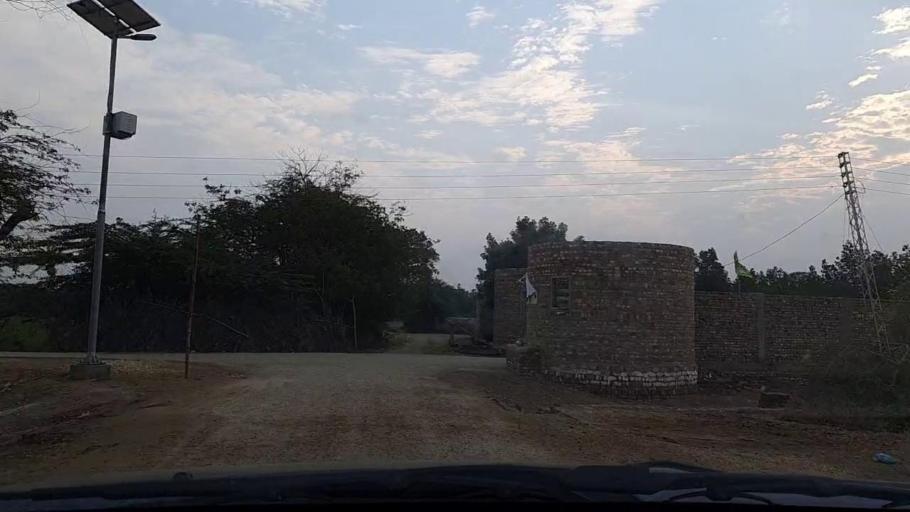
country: PK
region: Sindh
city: Pithoro
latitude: 25.6243
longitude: 69.4157
